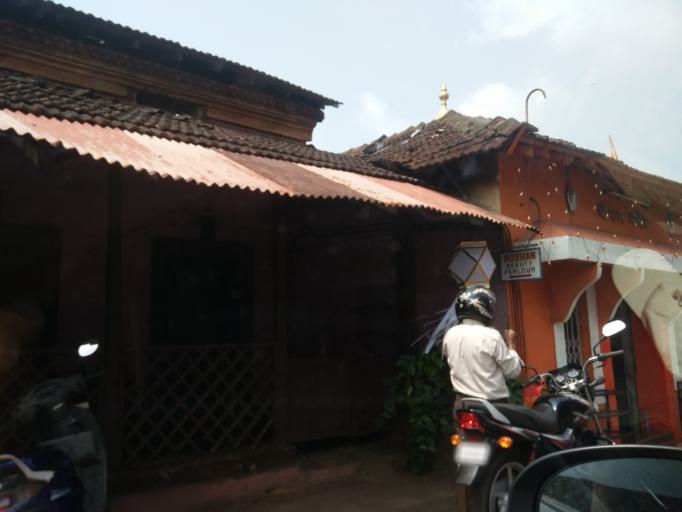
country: IN
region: Goa
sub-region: South Goa
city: Madgaon
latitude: 15.2800
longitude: 73.9570
